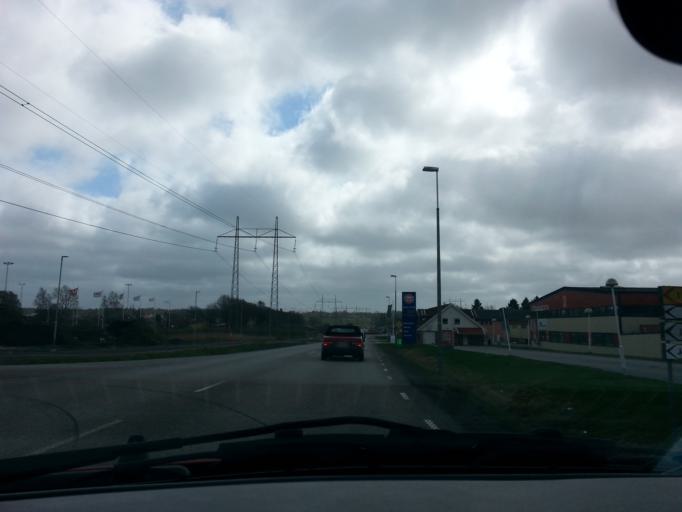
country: SE
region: Vaestra Goetaland
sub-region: Lerums Kommun
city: Grabo
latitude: 57.8412
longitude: 12.2873
